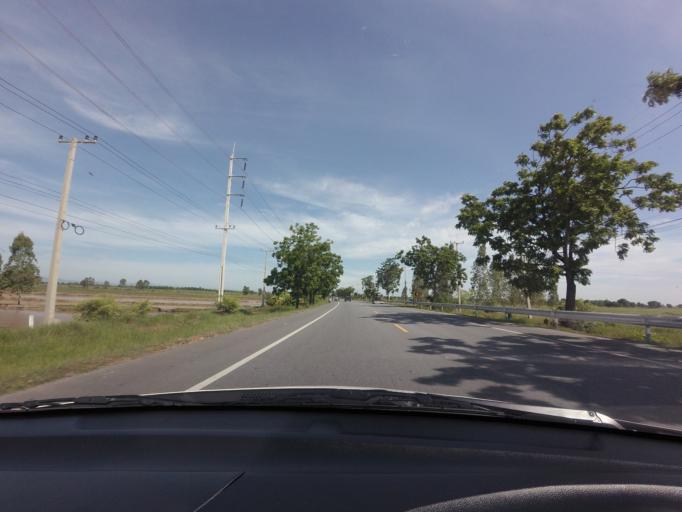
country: TH
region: Suphan Buri
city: Nong Yasai
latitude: 14.7171
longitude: 99.8312
